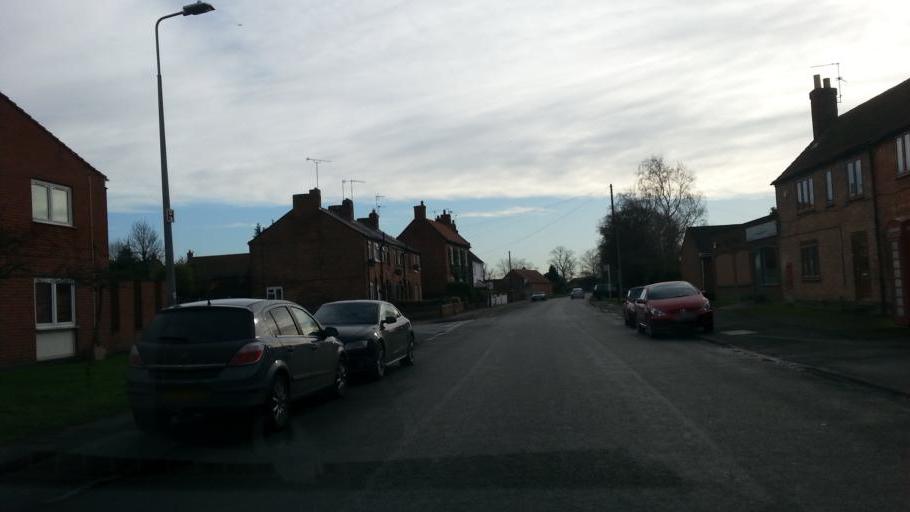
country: GB
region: England
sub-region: Nottinghamshire
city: Farndon
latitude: 53.0581
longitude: -0.8532
